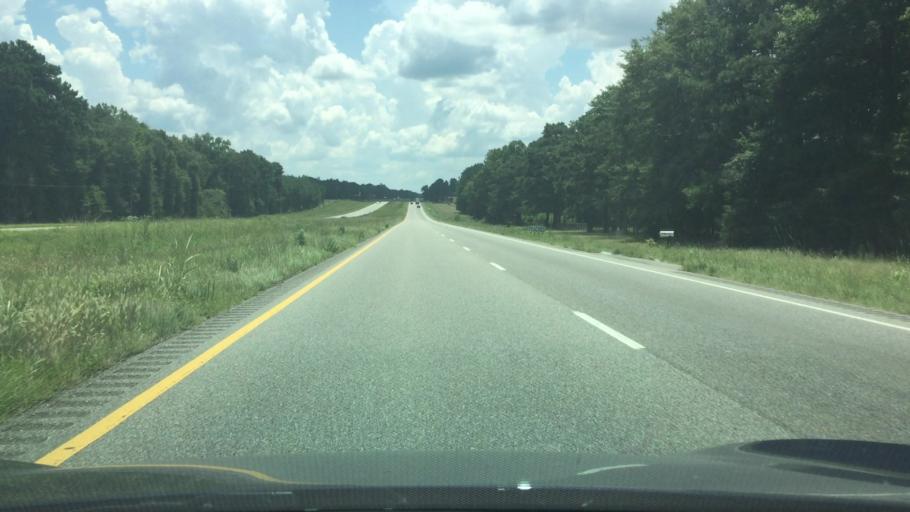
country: US
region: Alabama
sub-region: Montgomery County
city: Taylor
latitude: 32.0585
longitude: -86.0498
